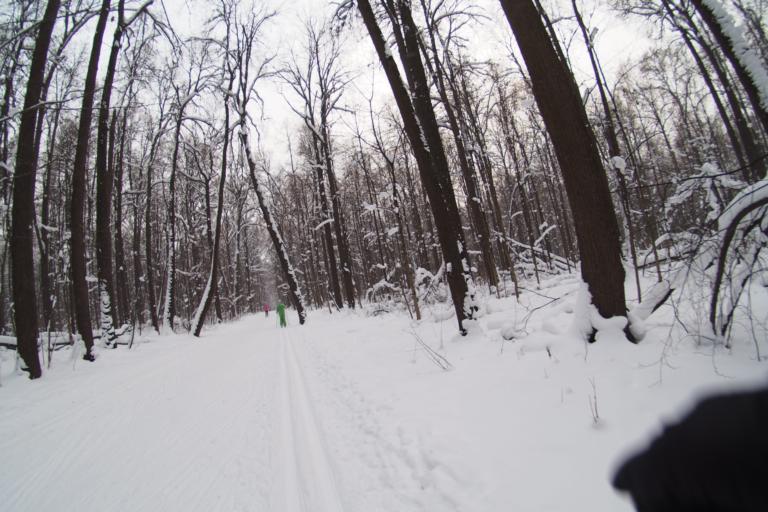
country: RU
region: Moskovskaya
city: Izmaylovo
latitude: 55.7711
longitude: 37.7772
